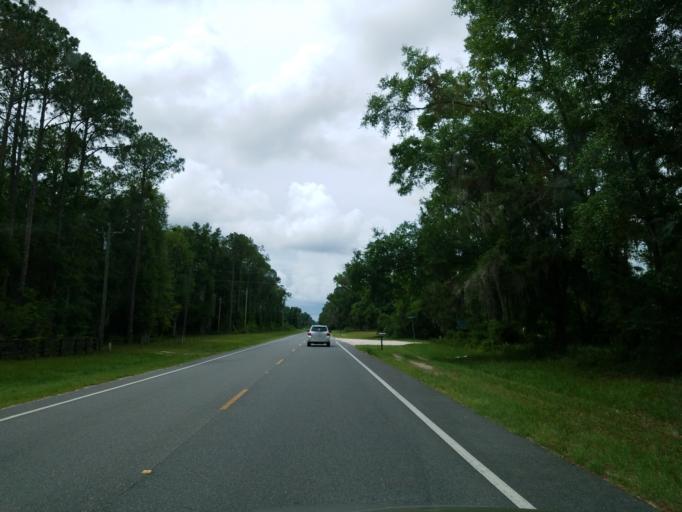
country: US
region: Florida
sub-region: Alachua County
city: High Springs
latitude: 29.8995
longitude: -82.4977
